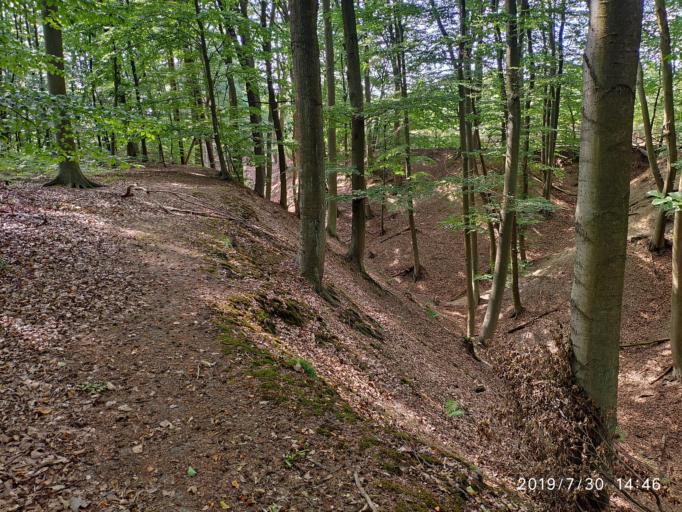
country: PL
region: Lubusz
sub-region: Powiat krosnienski
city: Bytnica
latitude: 52.1760
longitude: 15.2697
